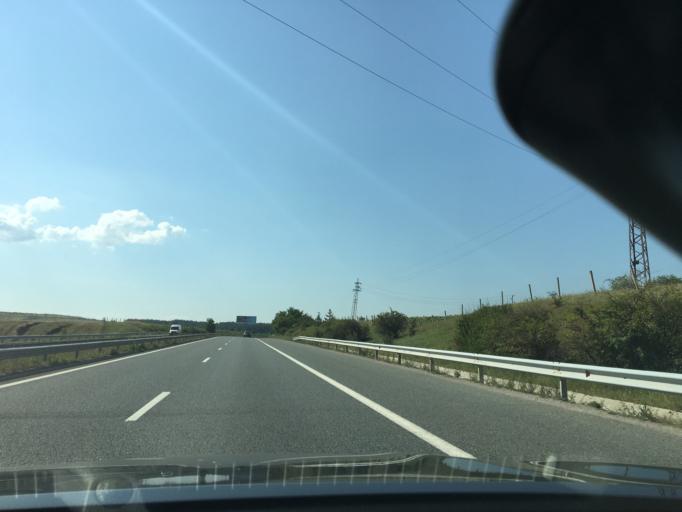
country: BG
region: Pernik
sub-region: Obshtina Pernik
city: Pernik
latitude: 42.5831
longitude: 23.1208
